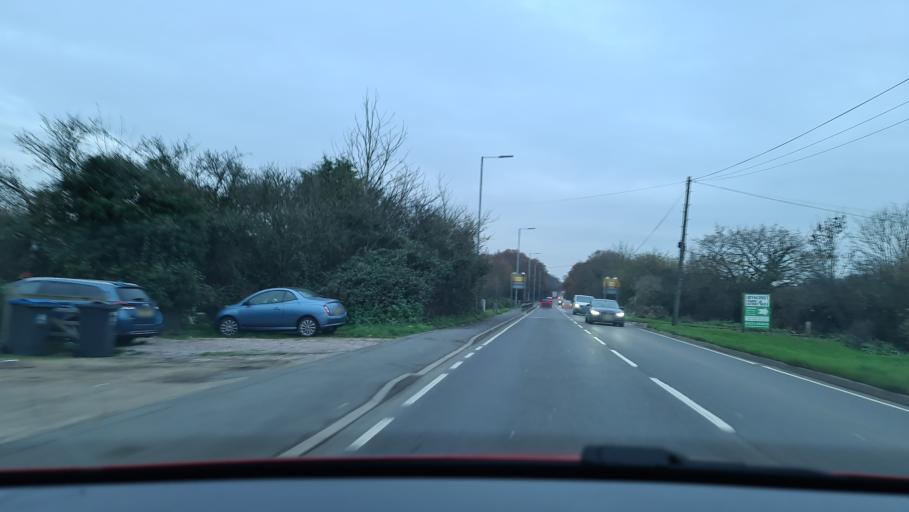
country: GB
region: England
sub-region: Greater London
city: Chessington
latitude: 51.3364
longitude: -0.3207
